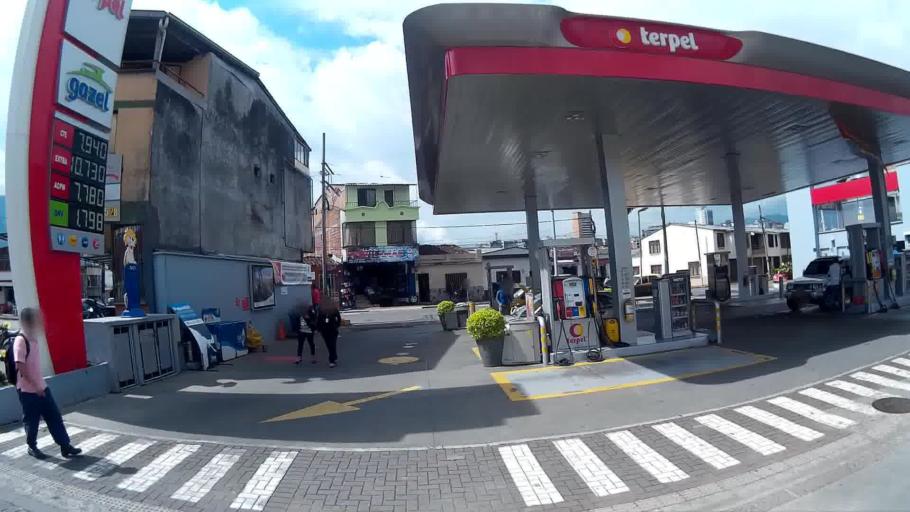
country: CO
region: Risaralda
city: Pereira
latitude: 4.8114
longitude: -75.7040
